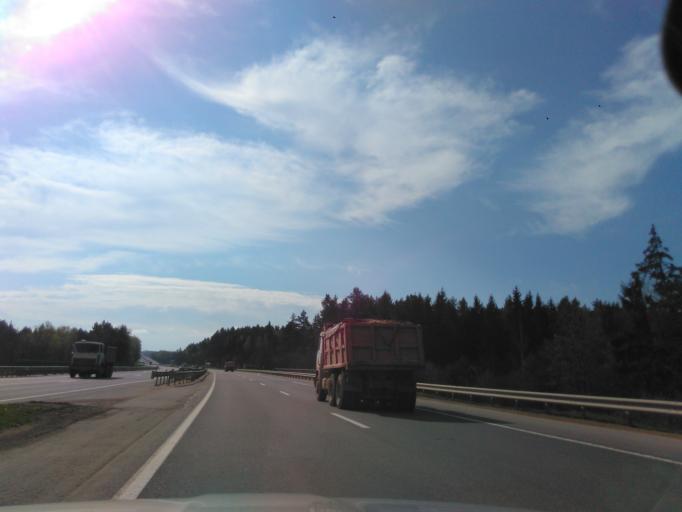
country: BY
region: Minsk
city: Rakaw
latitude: 53.9452
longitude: 27.1229
